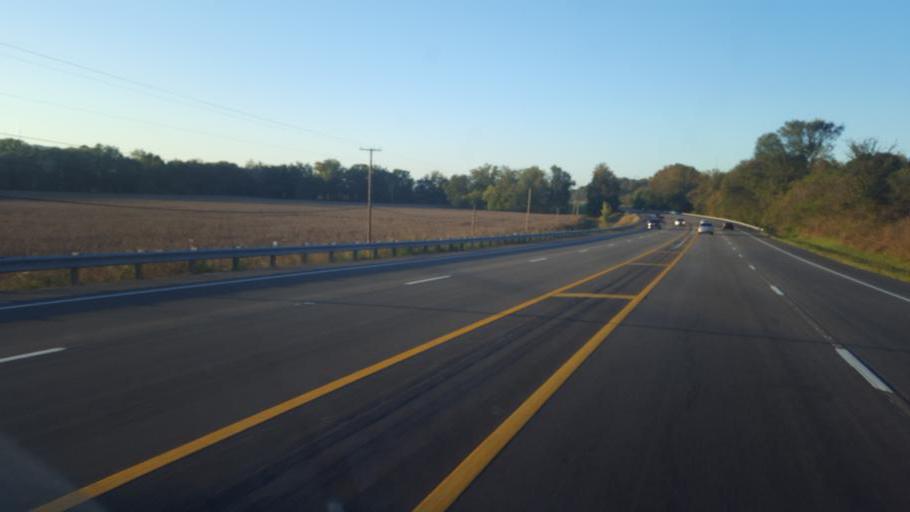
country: US
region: Ohio
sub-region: Scioto County
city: Lucasville
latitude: 38.8526
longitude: -82.9868
